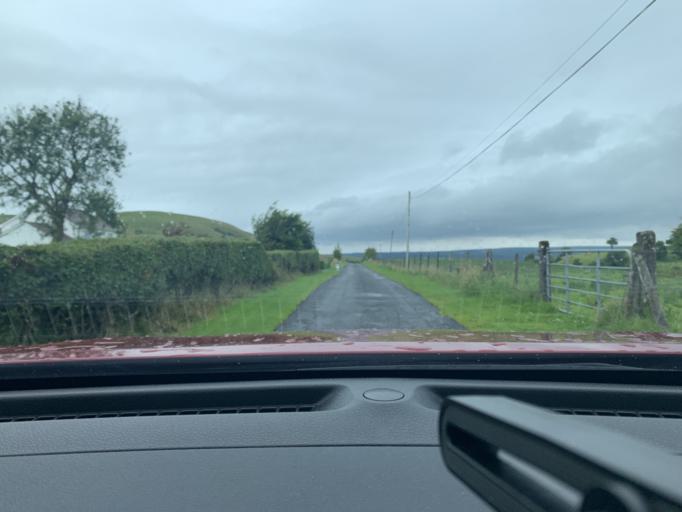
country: GB
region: Northern Ireland
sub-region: Fermanagh District
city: Enniskillen
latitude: 54.2668
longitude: -7.8507
